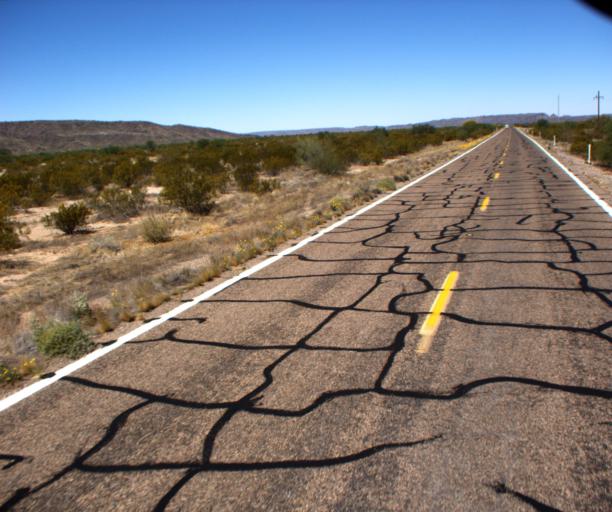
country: US
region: Arizona
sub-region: Pima County
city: Ajo
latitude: 32.4618
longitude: -112.8734
